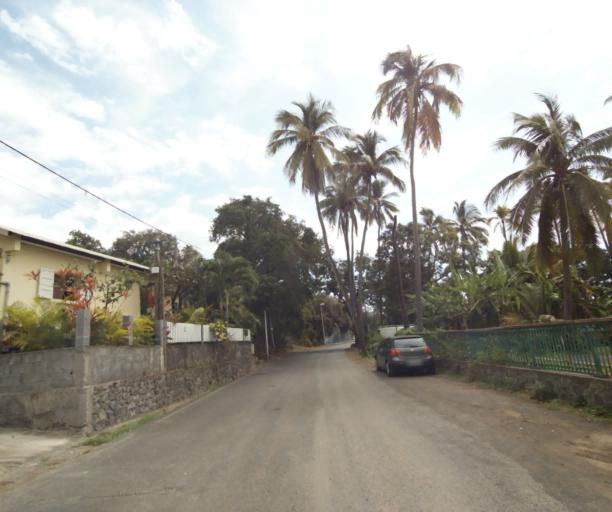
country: RE
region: Reunion
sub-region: Reunion
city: Saint-Paul
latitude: -21.0118
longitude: 55.2798
